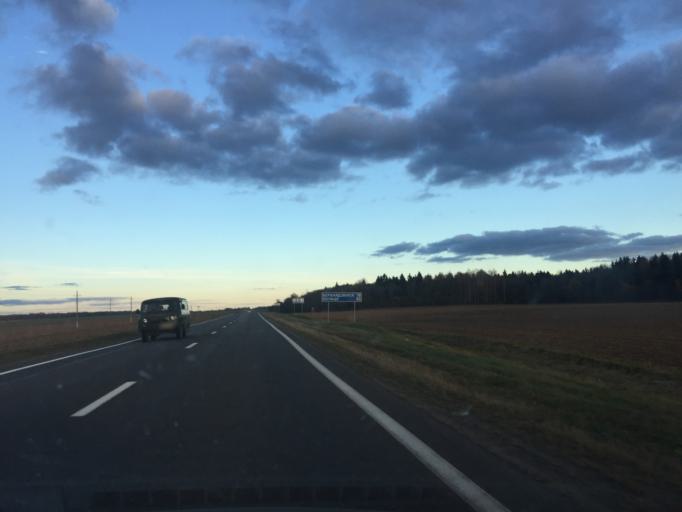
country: BY
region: Vitebsk
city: Vyerkhnyadzvinsk
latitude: 55.8224
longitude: 27.7391
